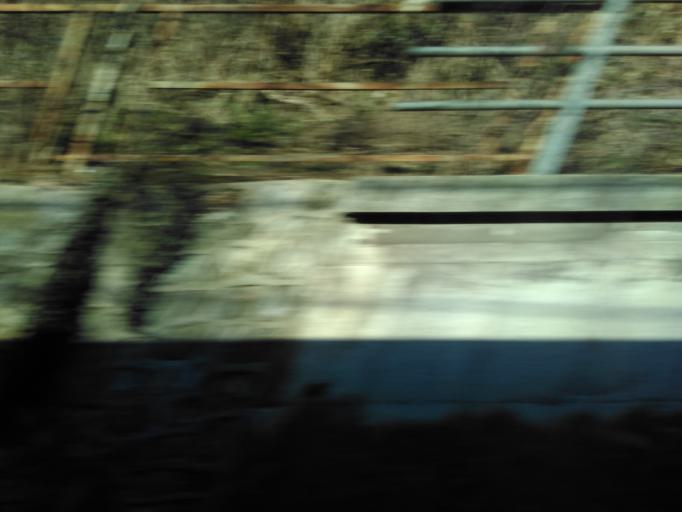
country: IT
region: Lombardy
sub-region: Provincia di Brescia
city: Lonato
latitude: 45.4632
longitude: 10.5024
